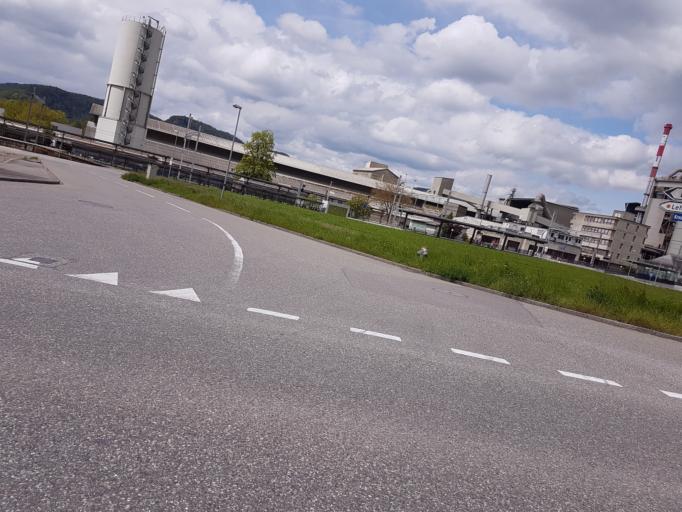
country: CH
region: Aargau
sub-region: Bezirk Brugg
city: Lauffohr (Brugg)
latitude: 47.5192
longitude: 8.2418
